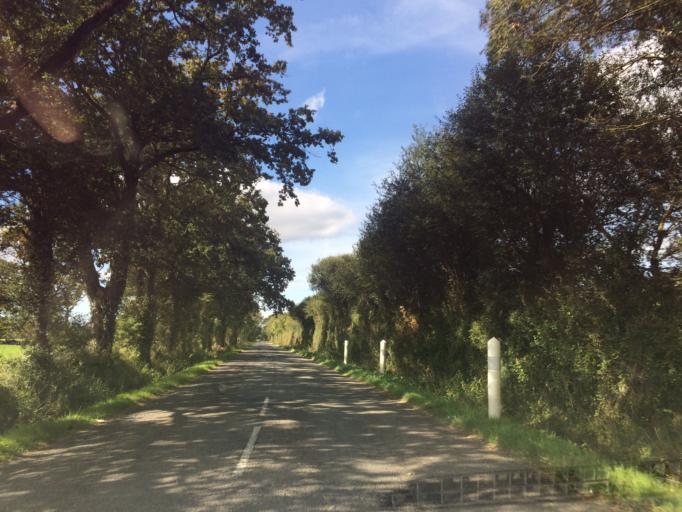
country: FR
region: Pays de la Loire
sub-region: Departement de la Loire-Atlantique
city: Chemere
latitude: 47.1150
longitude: -1.8994
